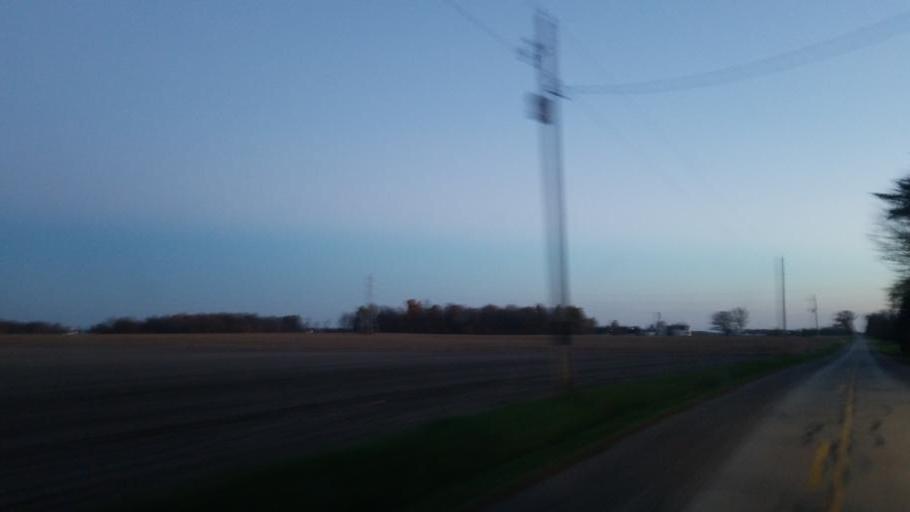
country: US
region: Ohio
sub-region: Crawford County
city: Crestline
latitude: 40.8583
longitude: -82.7442
